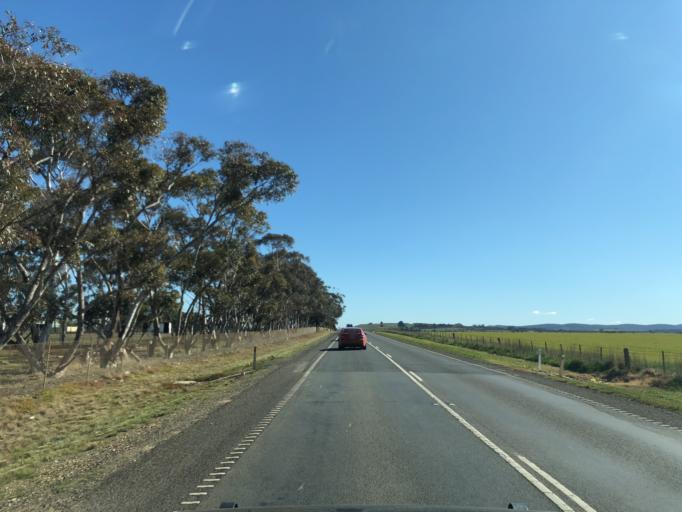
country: AU
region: Victoria
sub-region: Hume
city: Diggers Rest
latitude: -37.6261
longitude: 144.6760
